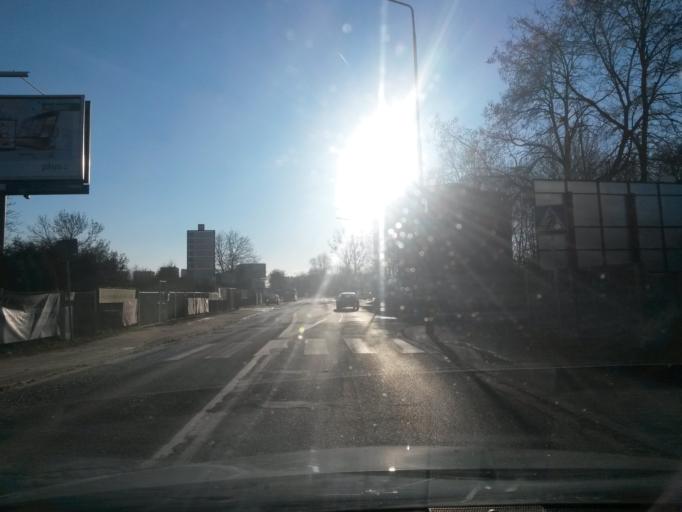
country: PL
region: Greater Poland Voivodeship
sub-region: Poznan
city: Poznan
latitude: 52.4394
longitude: 16.9119
